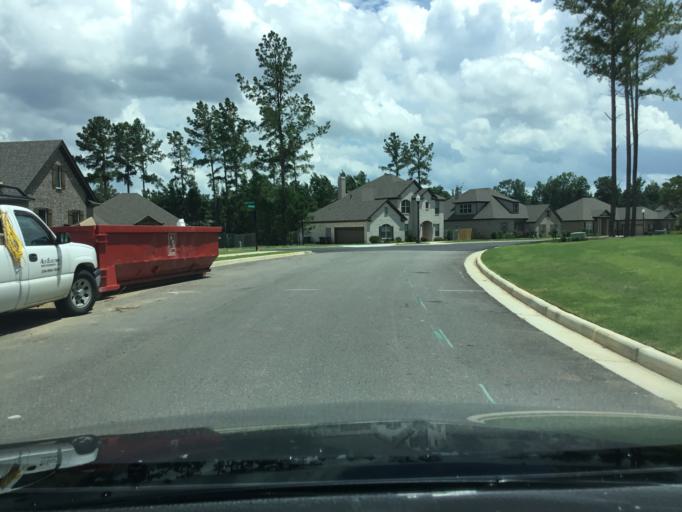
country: US
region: Alabama
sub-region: Montgomery County
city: Pike Road
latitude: 32.3388
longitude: -86.0797
